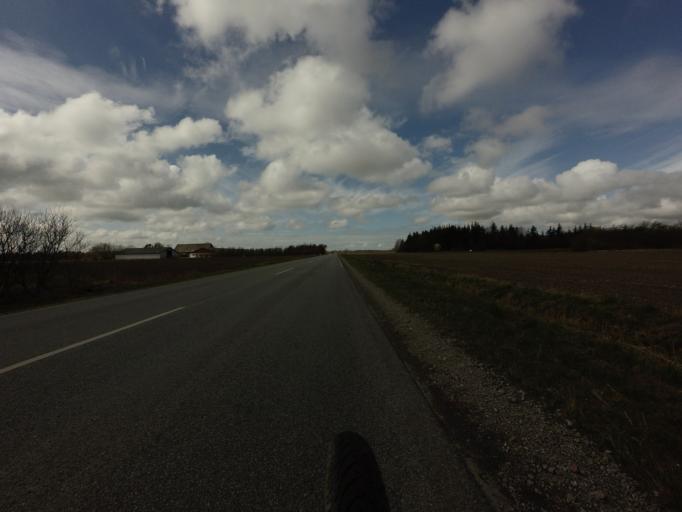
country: DK
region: North Denmark
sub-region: Hjorring Kommune
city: Vra
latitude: 57.3574
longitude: 9.8792
